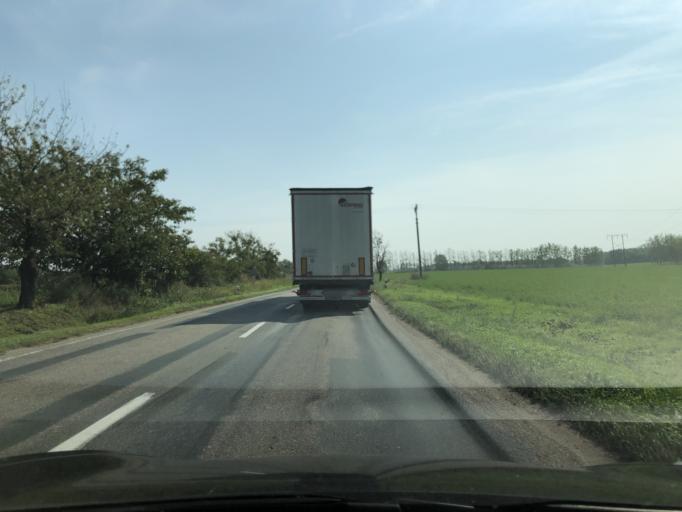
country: CZ
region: South Moravian
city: Brezi
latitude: 48.8211
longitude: 16.5751
